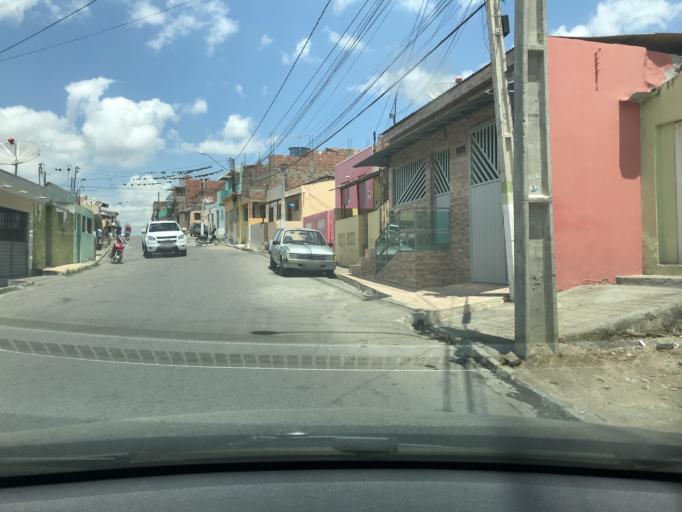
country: BR
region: Pernambuco
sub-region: Bezerros
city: Bezerros
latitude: -8.2353
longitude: -35.7470
